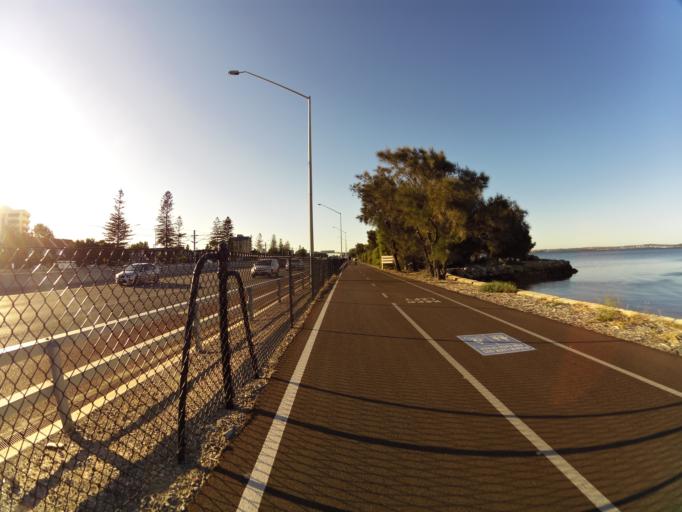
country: AU
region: Western Australia
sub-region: South Perth
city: South Perth
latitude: -31.9731
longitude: 115.8474
